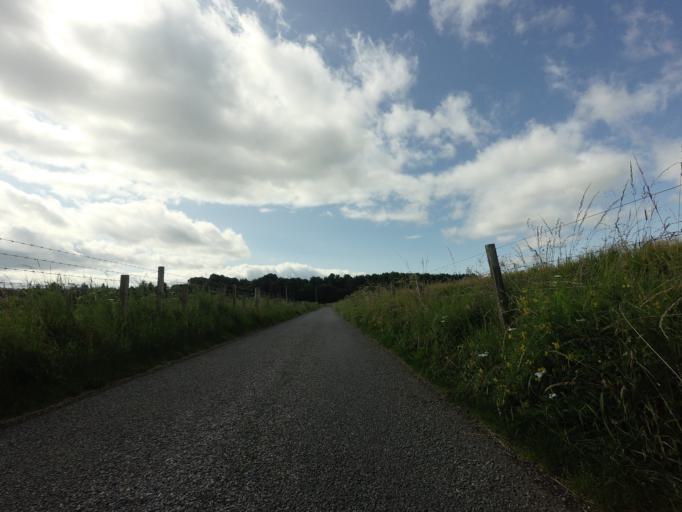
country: GB
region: Scotland
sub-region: Highland
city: Nairn
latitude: 57.5704
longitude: -3.8678
